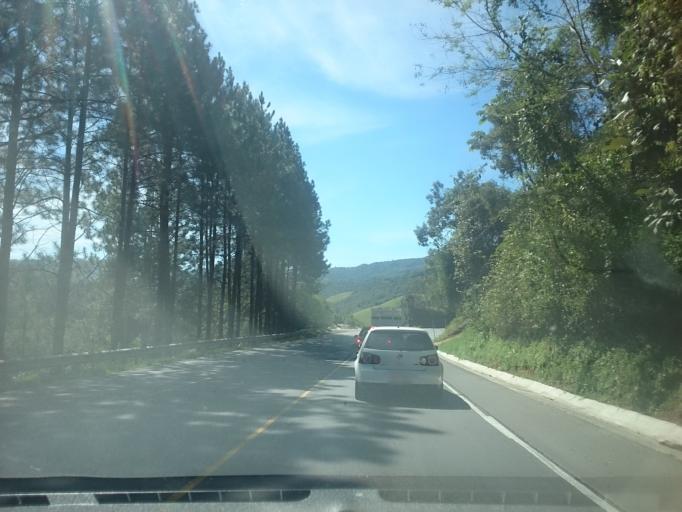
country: BR
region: Santa Catarina
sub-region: Santo Amaro Da Imperatriz
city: Santo Amaro da Imperatriz
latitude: -27.7152
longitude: -48.9405
